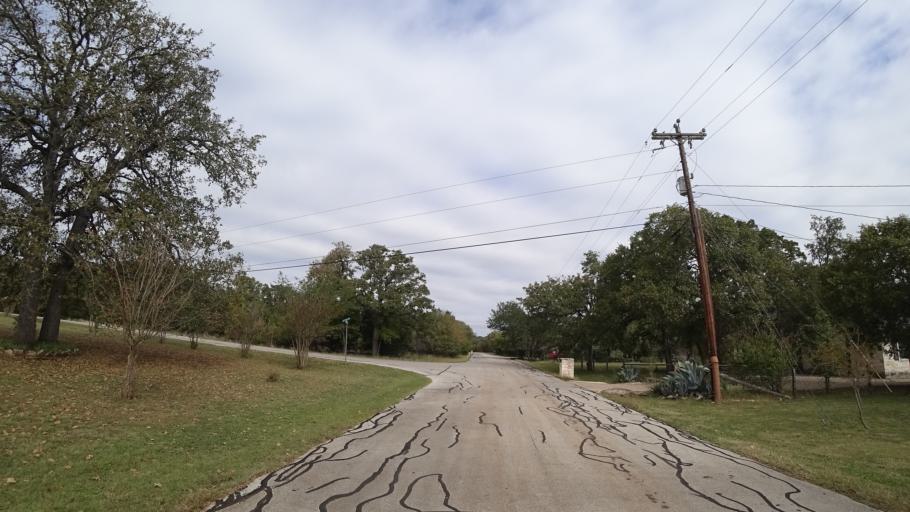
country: US
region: Texas
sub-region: Travis County
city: Shady Hollow
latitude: 30.1345
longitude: -97.8948
